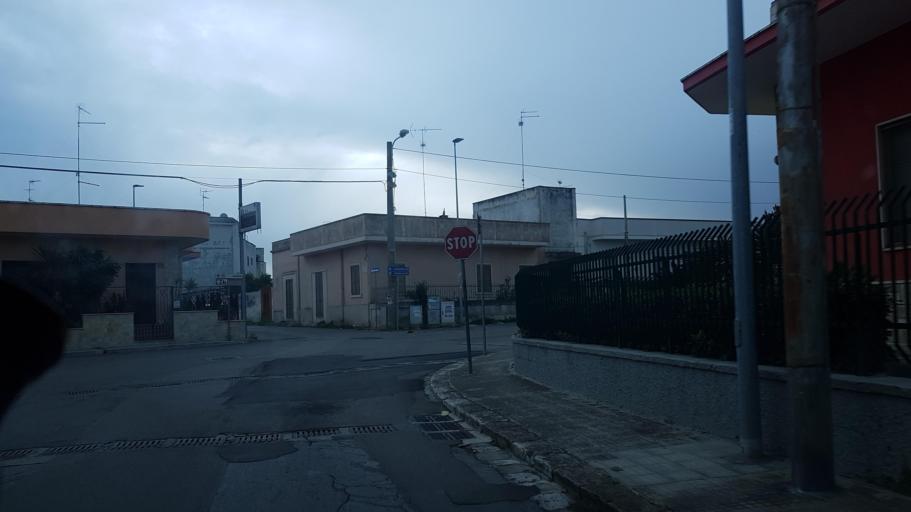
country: IT
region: Apulia
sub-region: Provincia di Lecce
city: Merine
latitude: 40.3354
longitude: 18.2212
